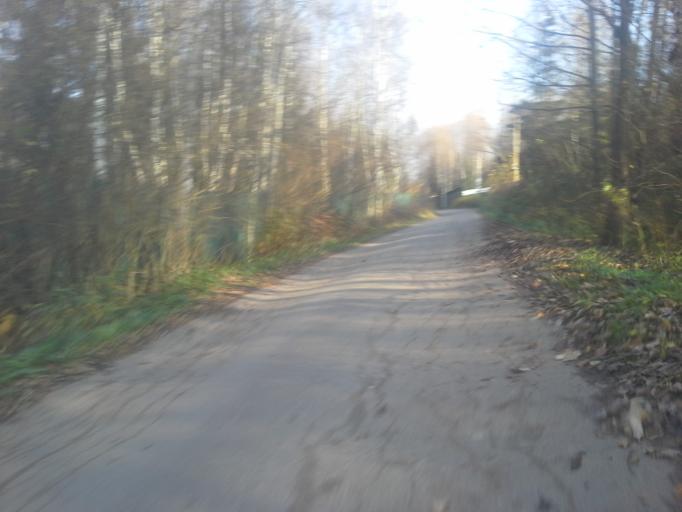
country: RU
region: Moskovskaya
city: Krasnoznamensk
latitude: 55.5748
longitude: 37.0097
